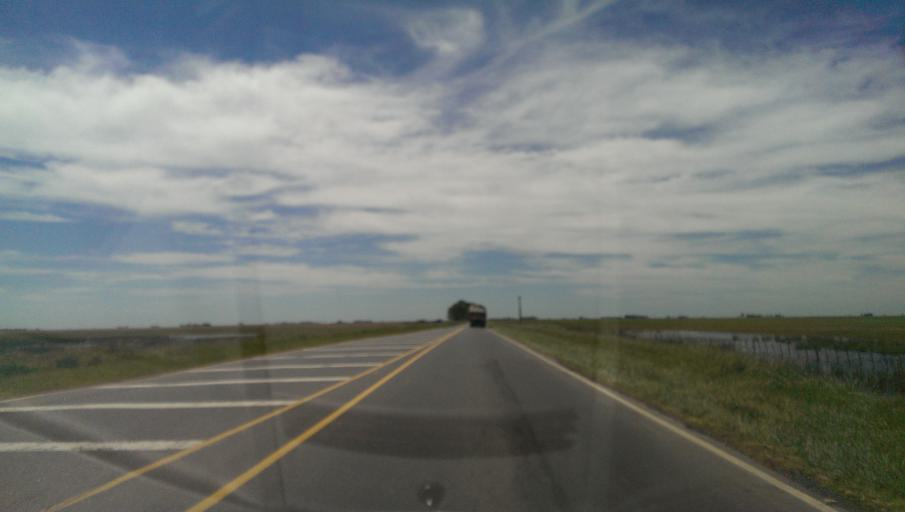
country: AR
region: Buenos Aires
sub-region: Partido de General La Madrid
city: General La Madrid
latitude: -37.4251
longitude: -61.0669
